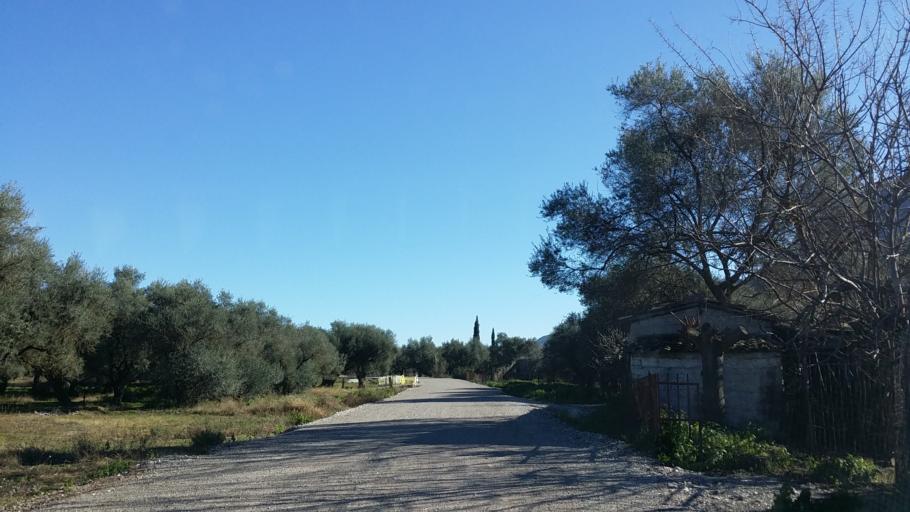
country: GR
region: West Greece
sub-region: Nomos Achaias
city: Temeni
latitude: 38.1931
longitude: 22.1833
